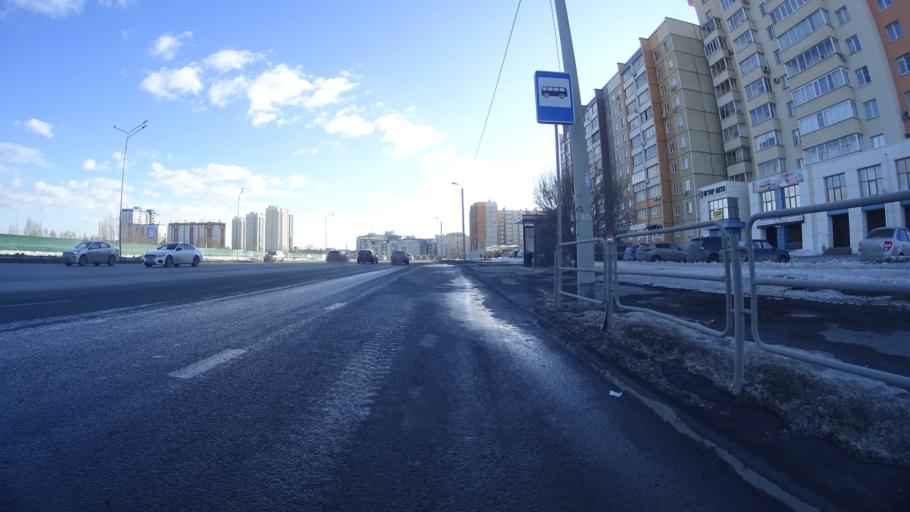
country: RU
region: Chelyabinsk
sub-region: Gorod Chelyabinsk
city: Chelyabinsk
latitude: 55.1627
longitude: 61.3023
